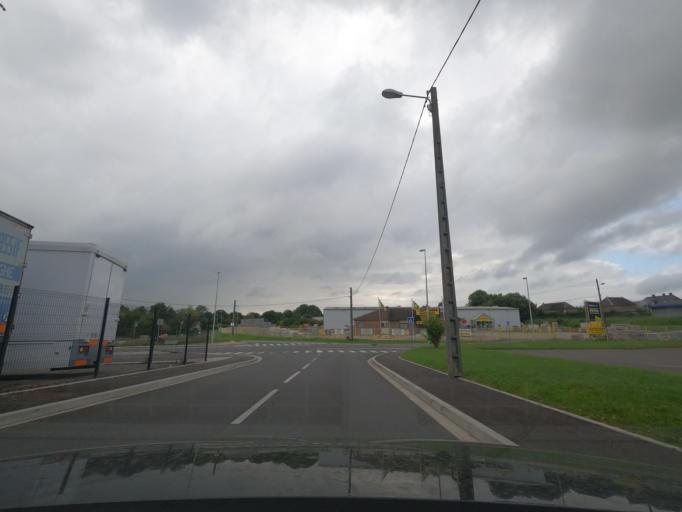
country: FR
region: Haute-Normandie
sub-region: Departement de la Seine-Maritime
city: Forges-les-Eaux
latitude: 49.6110
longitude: 1.5553
